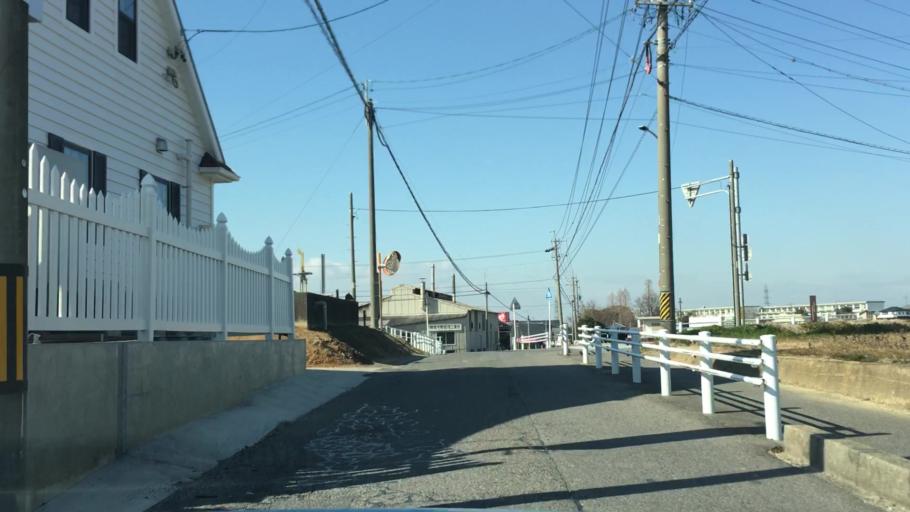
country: JP
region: Aichi
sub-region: Toyota-shi
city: Toyota
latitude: 35.0346
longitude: 137.1246
